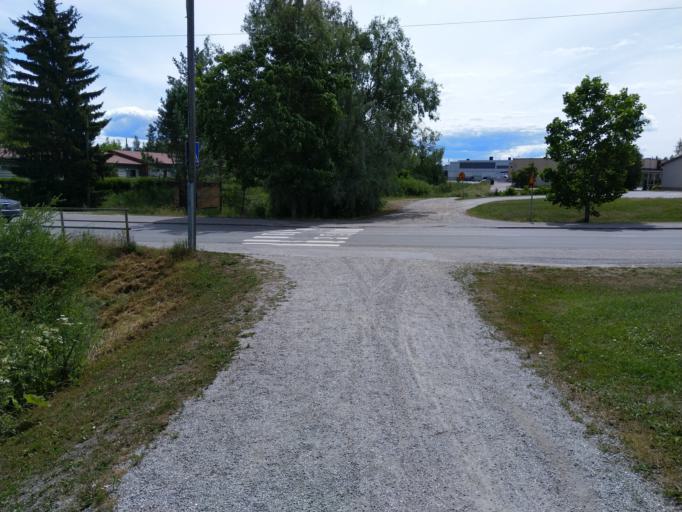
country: FI
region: Varsinais-Suomi
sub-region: Salo
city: Halikko
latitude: 60.3982
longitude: 23.0819
